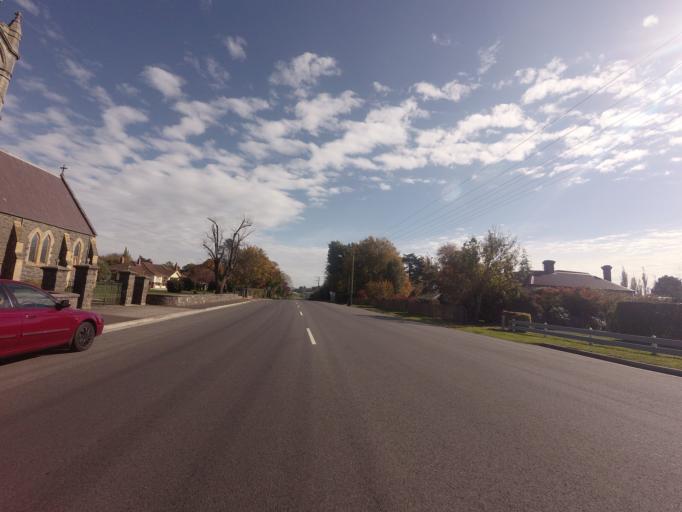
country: AU
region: Tasmania
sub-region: Meander Valley
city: Westbury
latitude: -41.5261
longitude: 146.8328
